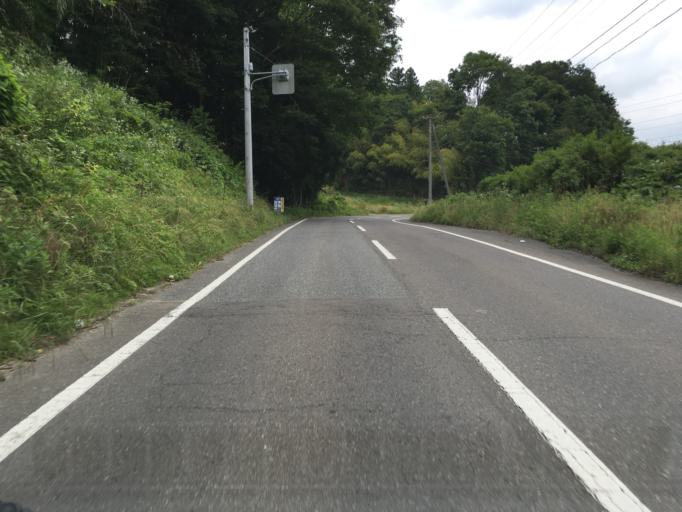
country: JP
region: Fukushima
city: Nihommatsu
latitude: 37.6203
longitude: 140.5397
